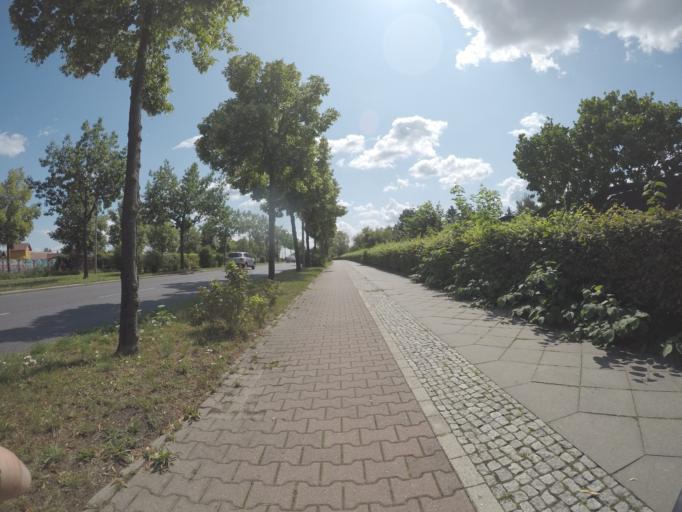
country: DE
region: Berlin
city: Marzahn
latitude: 52.5320
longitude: 13.5655
